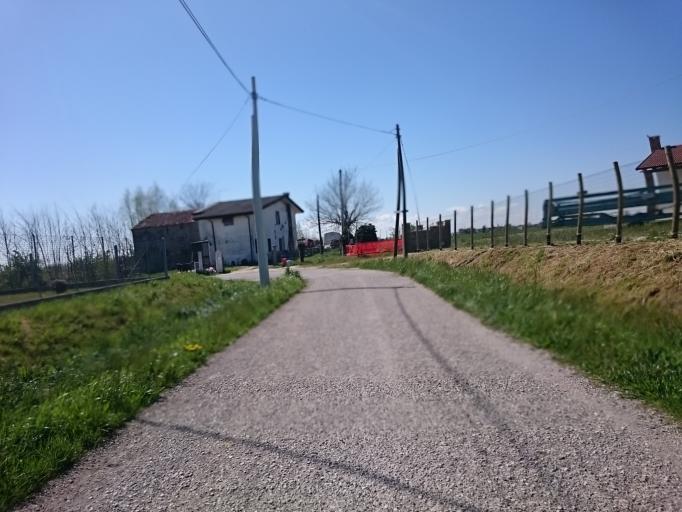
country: IT
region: Veneto
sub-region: Provincia di Padova
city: Polverara
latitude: 45.3091
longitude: 11.9707
